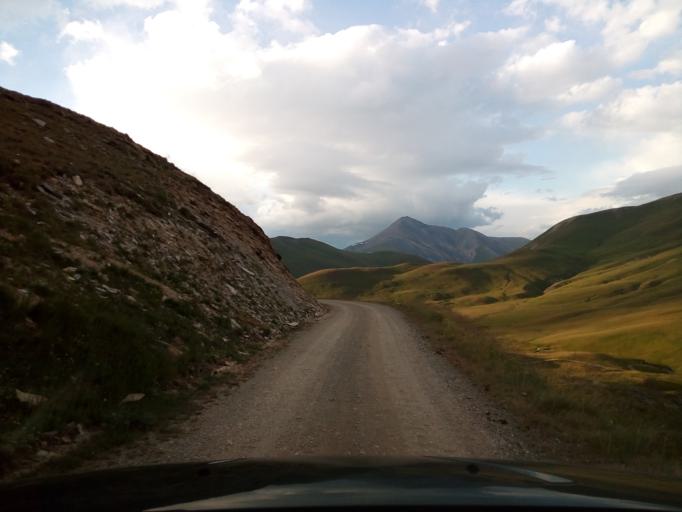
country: FR
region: Rhone-Alpes
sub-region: Departement de l'Isere
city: Mont-de-Lans
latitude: 45.0630
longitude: 6.2159
